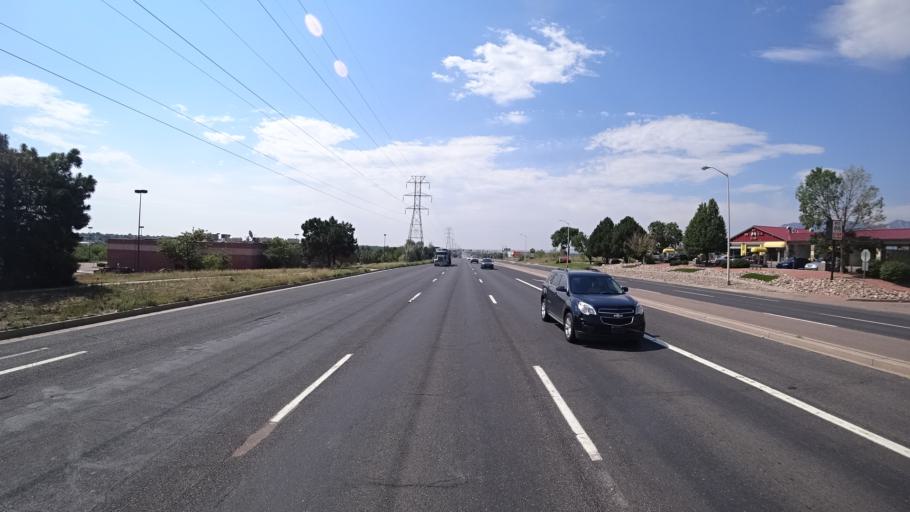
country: US
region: Colorado
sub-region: El Paso County
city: Stratmoor
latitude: 38.8117
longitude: -104.7574
